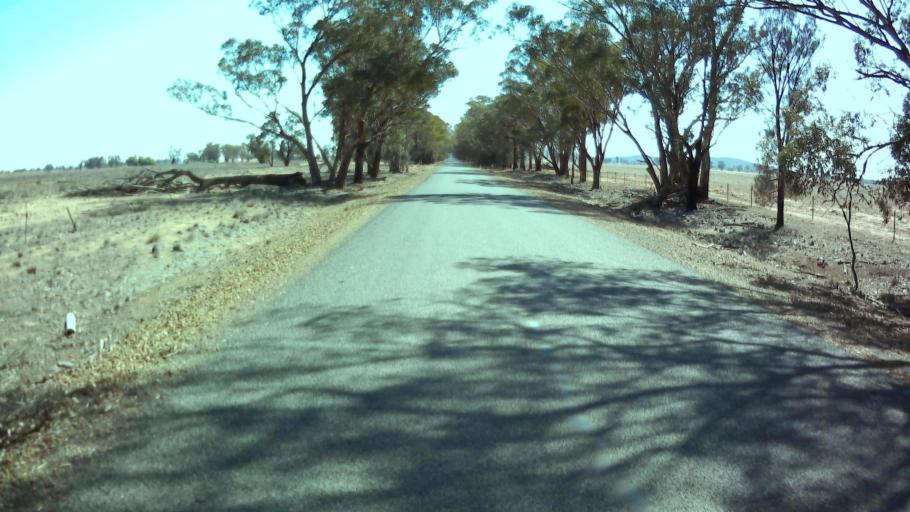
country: AU
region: New South Wales
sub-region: Weddin
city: Grenfell
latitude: -33.7270
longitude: 147.8925
